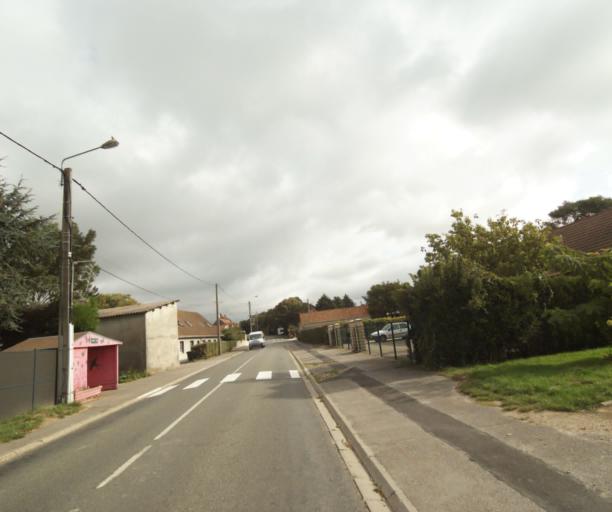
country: FR
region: Nord-Pas-de-Calais
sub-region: Departement du Pas-de-Calais
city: Etaples
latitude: 50.5262
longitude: 1.6787
